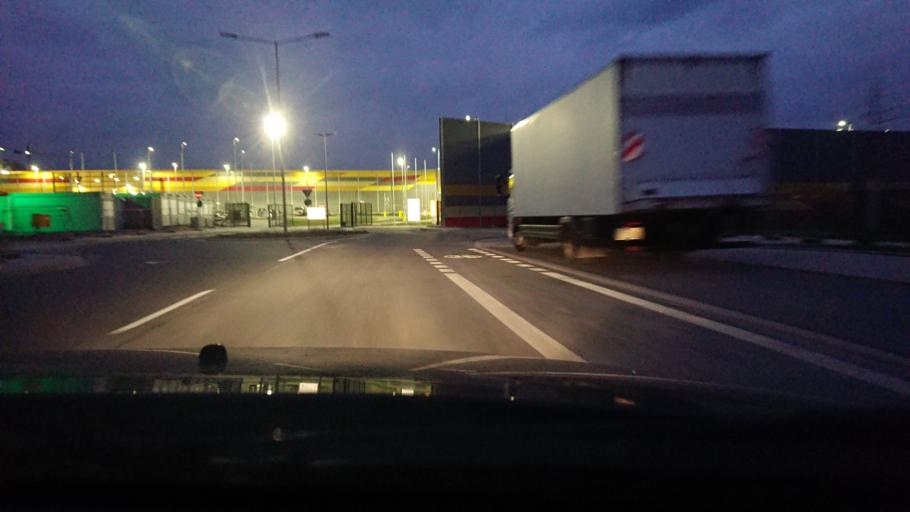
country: DE
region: North Rhine-Westphalia
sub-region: Regierungsbezirk Arnsberg
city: Bochum
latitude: 51.4646
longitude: 7.2606
